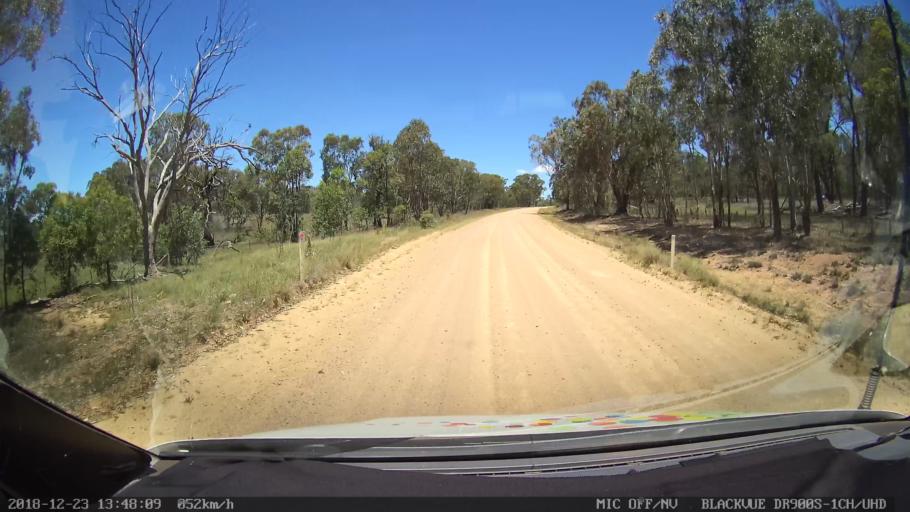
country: AU
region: New South Wales
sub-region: Tamworth Municipality
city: Manilla
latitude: -30.5152
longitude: 151.1162
